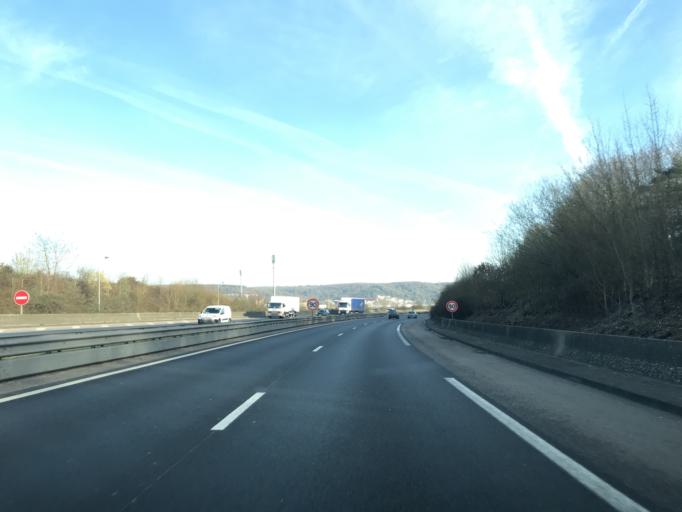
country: FR
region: Haute-Normandie
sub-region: Departement de la Seine-Maritime
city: Le Grand-Quevilly
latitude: 49.3958
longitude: 1.0336
